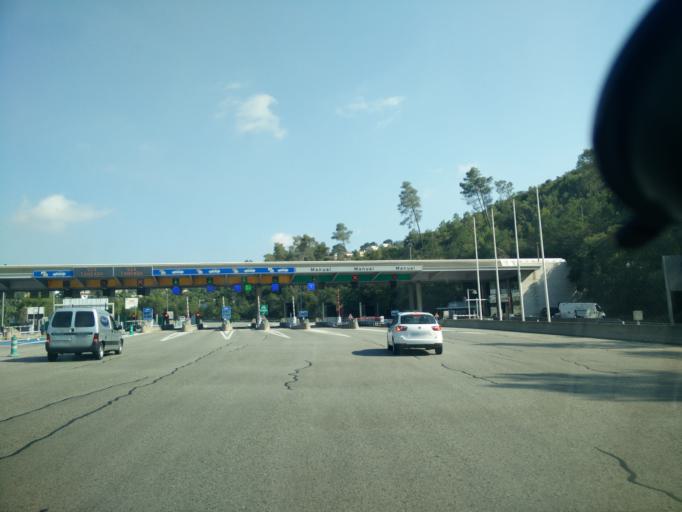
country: ES
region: Catalonia
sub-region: Provincia de Barcelona
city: Sant Cugat del Valles
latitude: 41.4367
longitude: 2.0756
